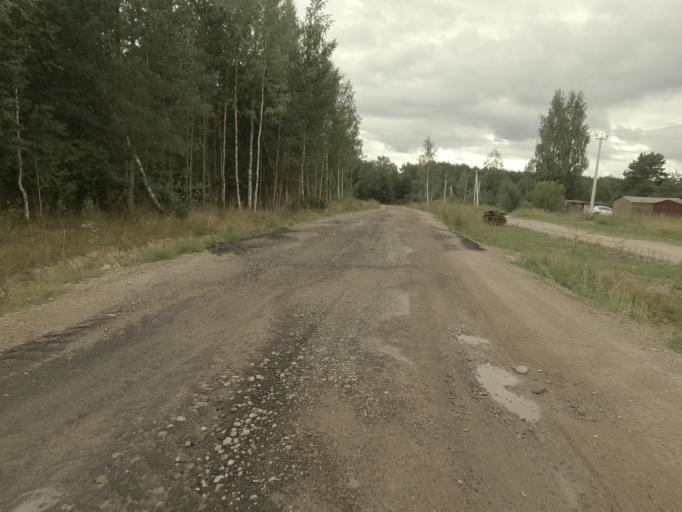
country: RU
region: Leningrad
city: Kirovsk
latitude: 59.8996
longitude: 31.0030
